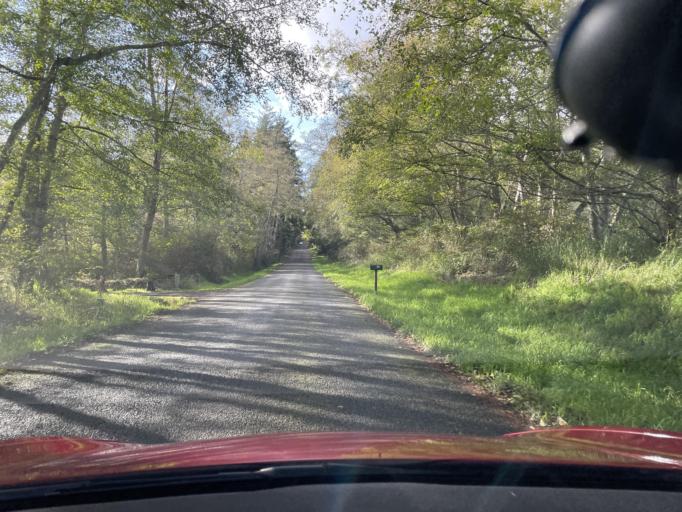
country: US
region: Washington
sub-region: San Juan County
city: Friday Harbor
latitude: 48.4818
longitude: -123.0365
